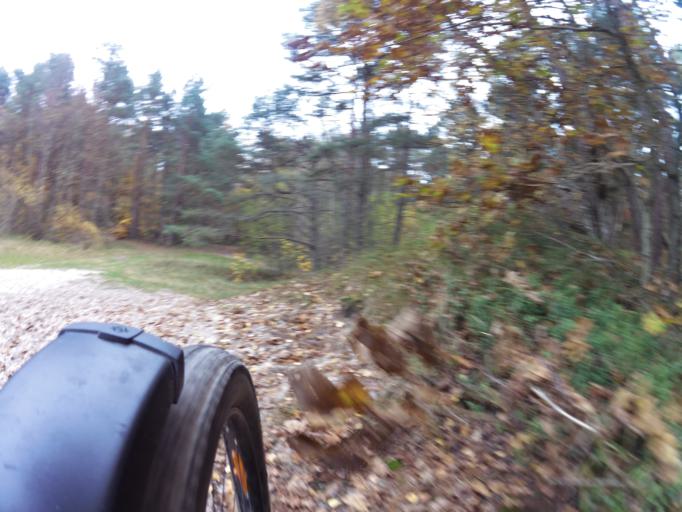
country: PL
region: Pomeranian Voivodeship
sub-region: Powiat pucki
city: Krokowa
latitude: 54.8309
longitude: 18.1436
